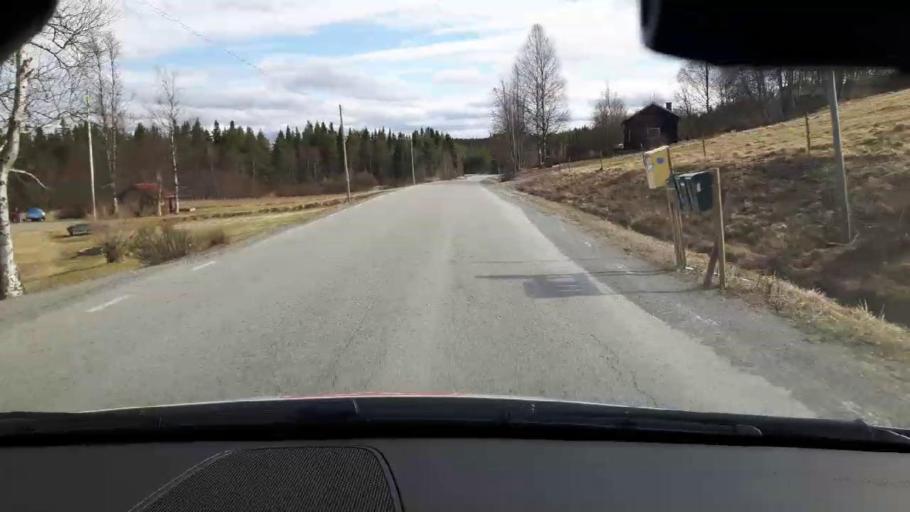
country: SE
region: Jaemtland
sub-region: Bergs Kommun
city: Hoverberg
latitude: 62.7256
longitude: 14.5999
